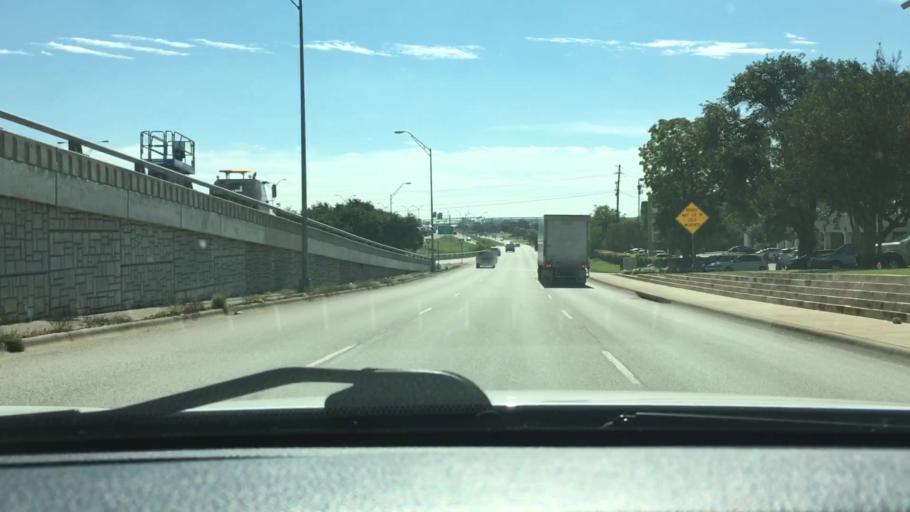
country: US
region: Texas
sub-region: Williamson County
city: Round Rock
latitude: 30.5091
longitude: -97.6865
